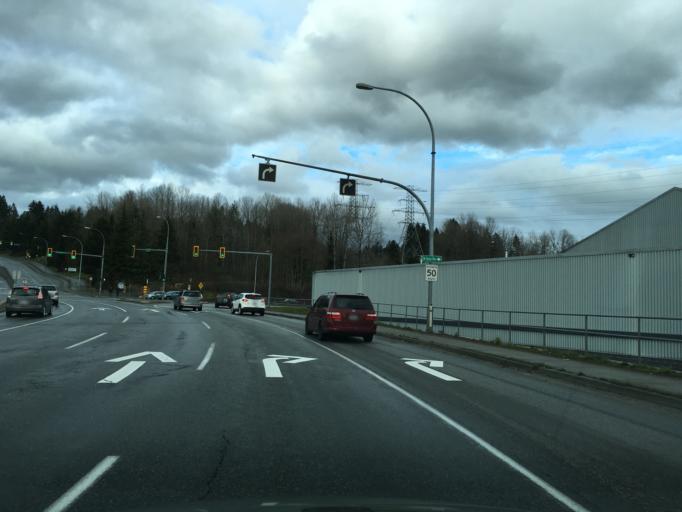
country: CA
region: British Columbia
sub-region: Fraser Valley Regional District
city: North Vancouver
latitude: 49.3116
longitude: -123.0259
